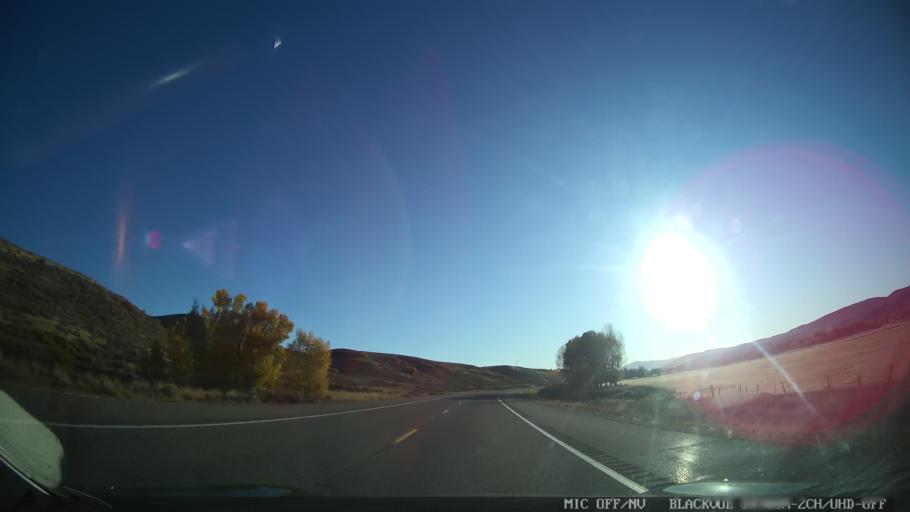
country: US
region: Colorado
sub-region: Grand County
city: Kremmling
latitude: 40.0678
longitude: -106.2700
